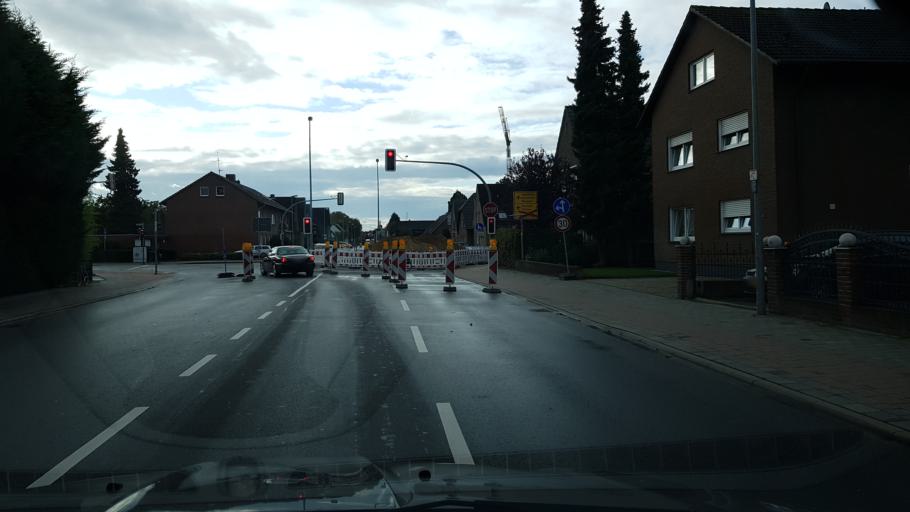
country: DE
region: North Rhine-Westphalia
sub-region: Regierungsbezirk Munster
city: Rhede
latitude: 51.8340
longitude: 6.6992
